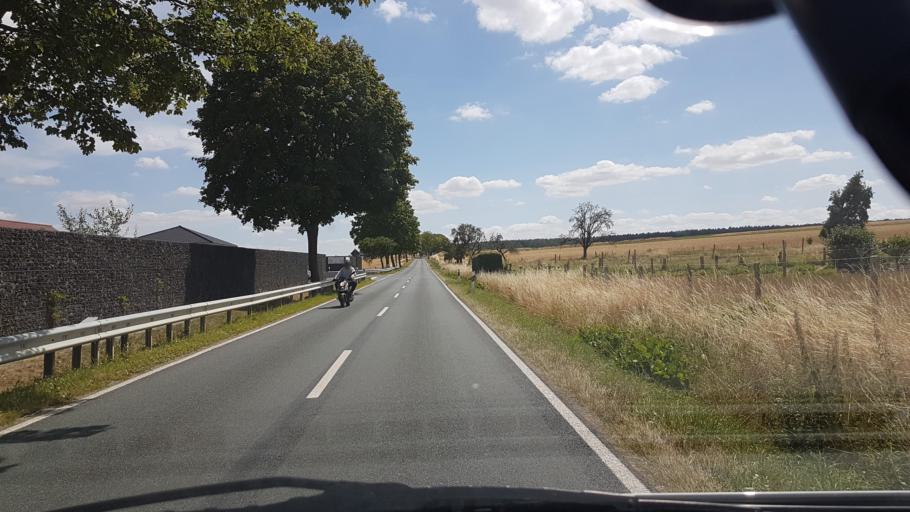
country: DE
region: Lower Saxony
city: Rabke
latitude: 52.1933
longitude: 10.8809
